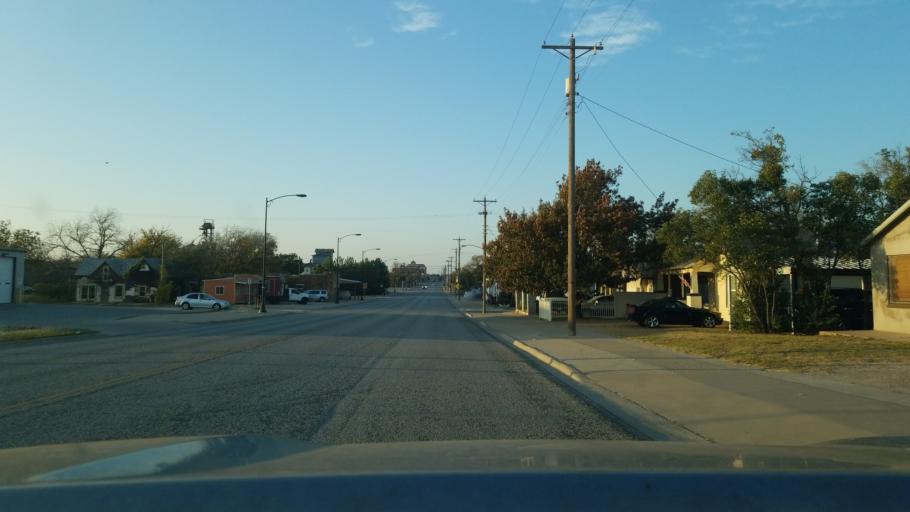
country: US
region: Texas
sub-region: Eastland County
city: Cisco
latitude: 32.3827
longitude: -98.9758
